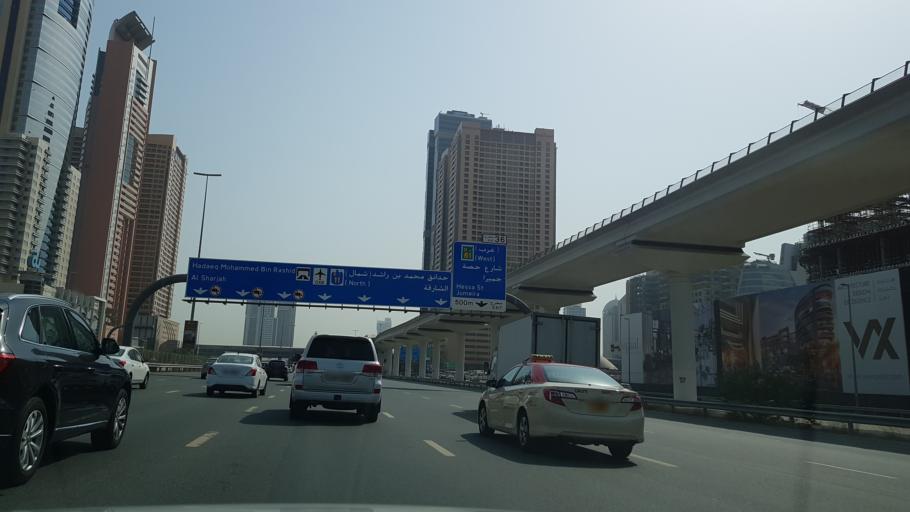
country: AE
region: Dubai
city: Dubai
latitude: 25.0987
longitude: 55.1694
